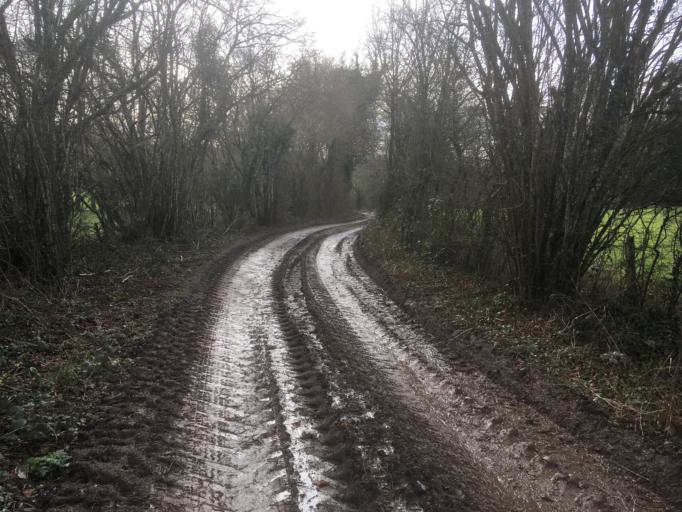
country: BE
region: Wallonia
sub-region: Province du Luxembourg
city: Erezee
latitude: 50.3164
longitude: 5.5064
